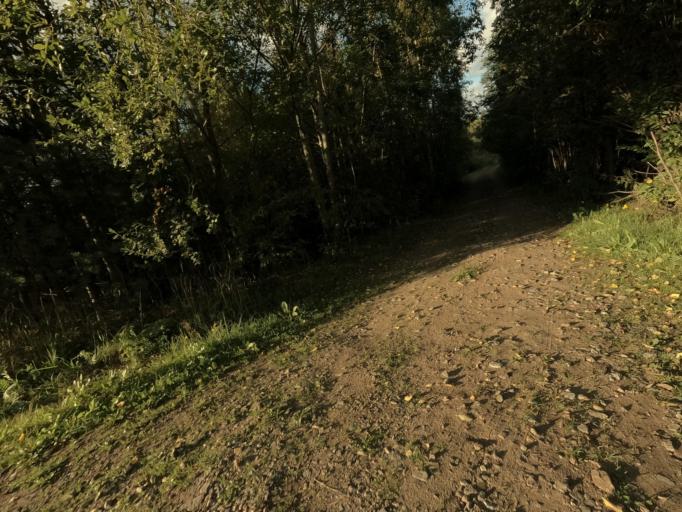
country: RU
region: Leningrad
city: Imeni Sverdlova
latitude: 59.8550
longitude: 30.7309
